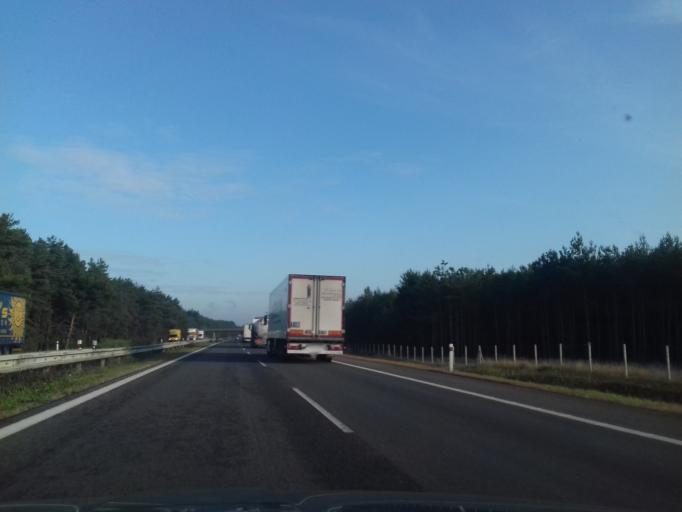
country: SK
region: Bratislavsky
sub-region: Okres Malacky
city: Malacky
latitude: 48.3917
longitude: 17.0253
